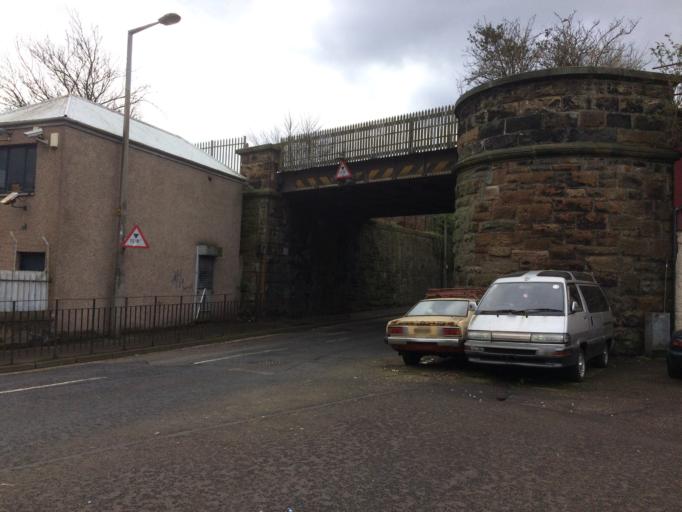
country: GB
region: Scotland
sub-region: West Lothian
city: Seafield
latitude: 55.9570
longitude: -3.1501
